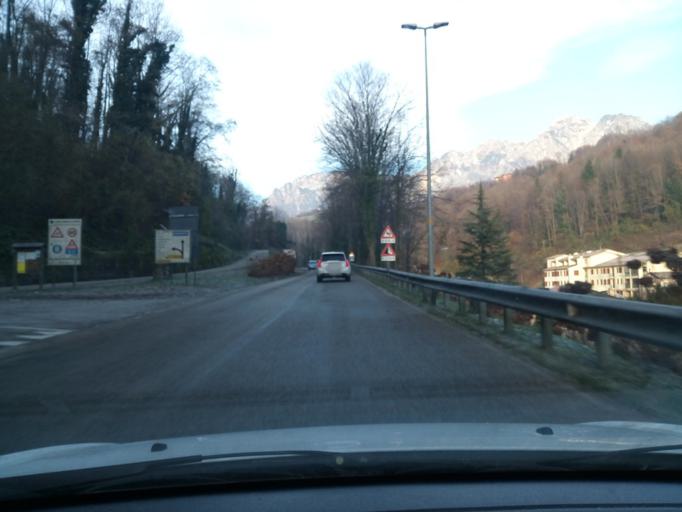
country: IT
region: Veneto
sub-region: Provincia di Vicenza
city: Valli del Pasubio
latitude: 45.7430
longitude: 11.2584
